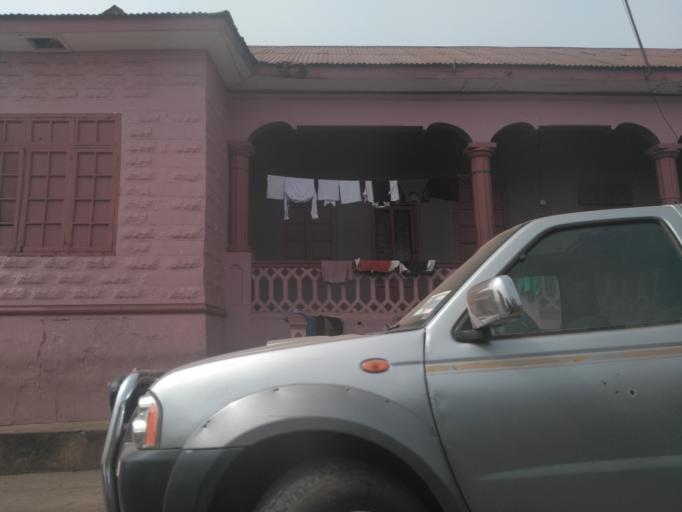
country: GH
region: Ashanti
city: Kumasi
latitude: 6.7052
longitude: -1.6223
